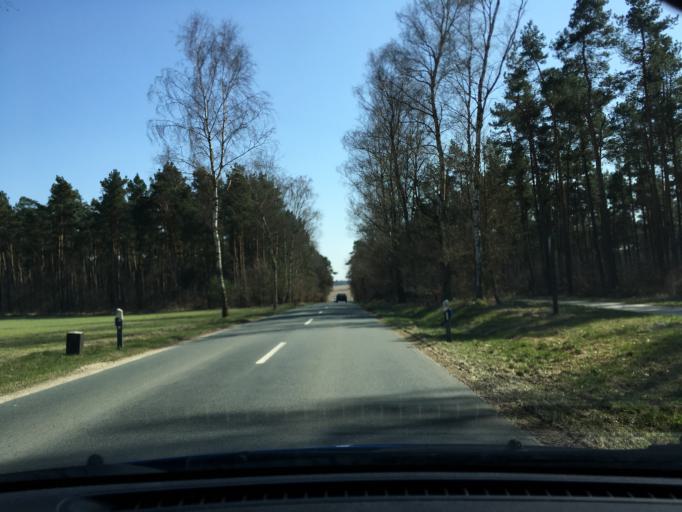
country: DE
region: Lower Saxony
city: Eimke
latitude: 52.9920
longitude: 10.3046
